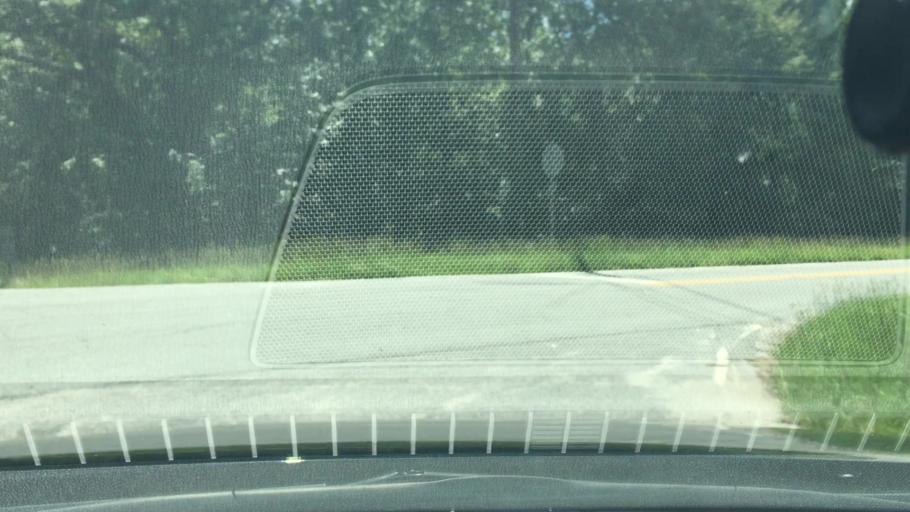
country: US
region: Georgia
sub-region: Putnam County
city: Jefferson
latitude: 33.3576
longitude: -83.2596
